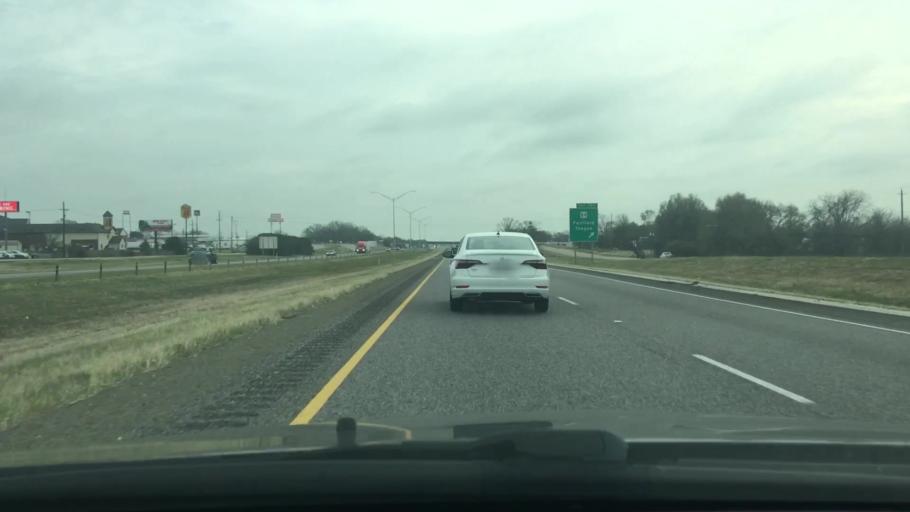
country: US
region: Texas
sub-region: Freestone County
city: Fairfield
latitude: 31.7217
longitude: -96.1789
